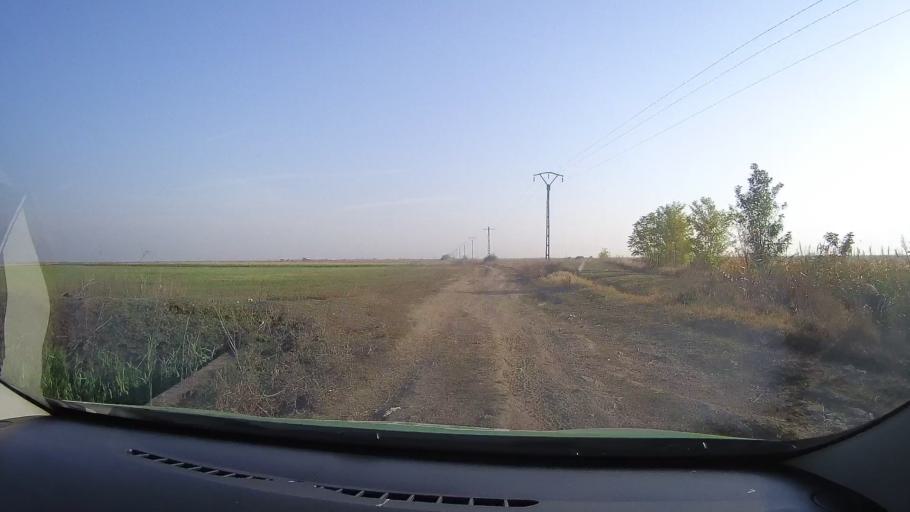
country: RO
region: Arad
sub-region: Comuna Graniceri
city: Graniceri
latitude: 46.5290
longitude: 21.3135
